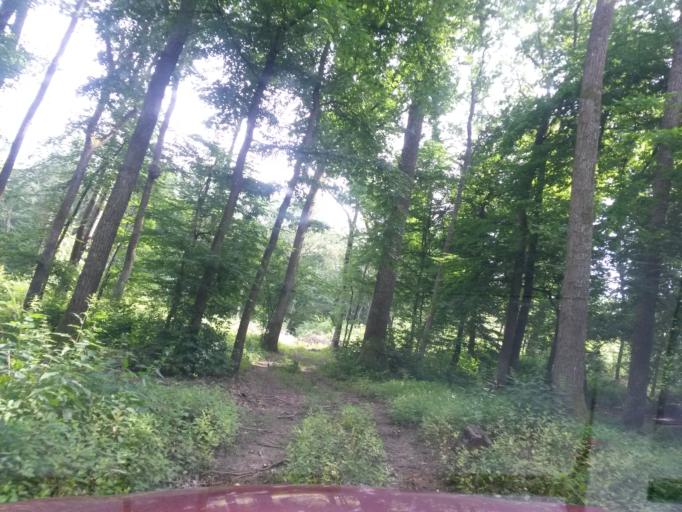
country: SK
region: Kosicky
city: Moldava nad Bodvou
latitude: 48.6417
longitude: 21.1019
